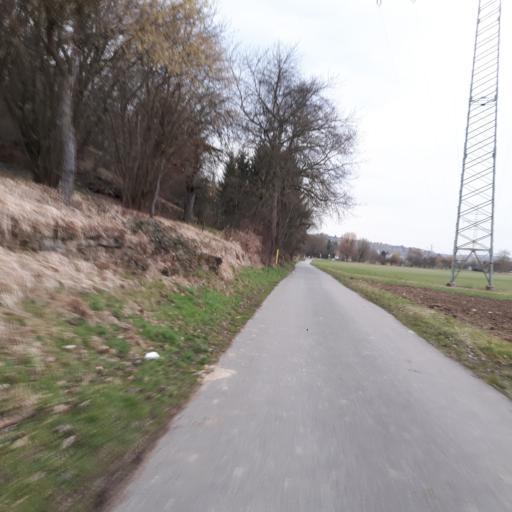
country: DE
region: Baden-Wuerttemberg
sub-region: Regierungsbezirk Stuttgart
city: Pleidelsheim
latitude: 48.9561
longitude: 9.1840
